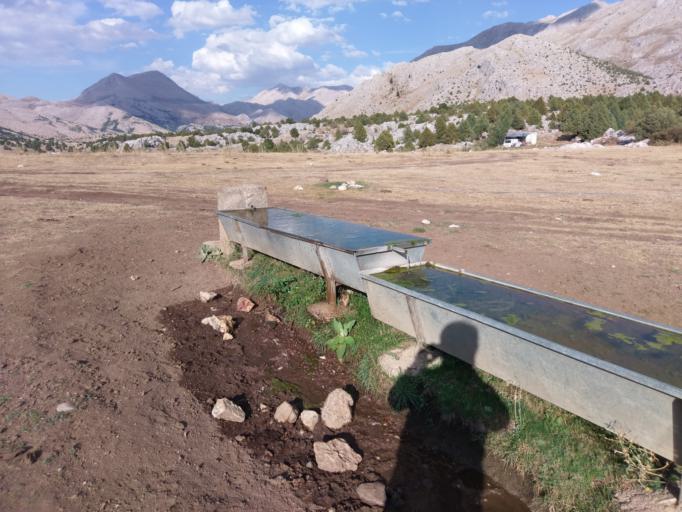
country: TR
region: Kayseri
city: Toklar
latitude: 38.3586
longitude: 36.1095
